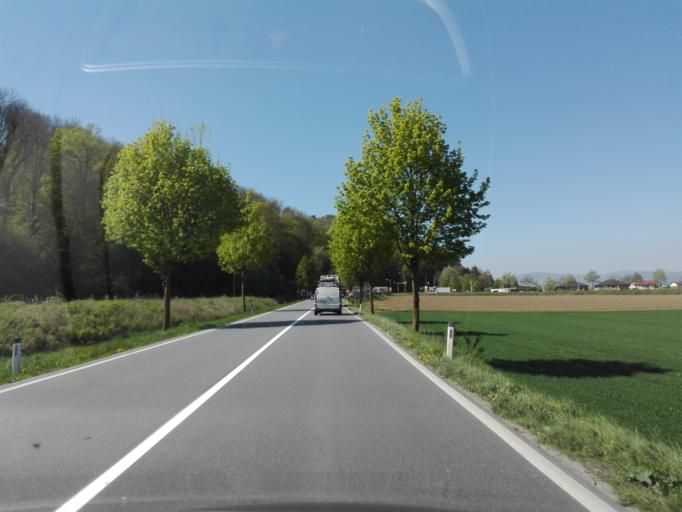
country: AT
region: Upper Austria
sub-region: Politischer Bezirk Linz-Land
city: Sankt Florian
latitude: 48.2400
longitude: 14.3648
